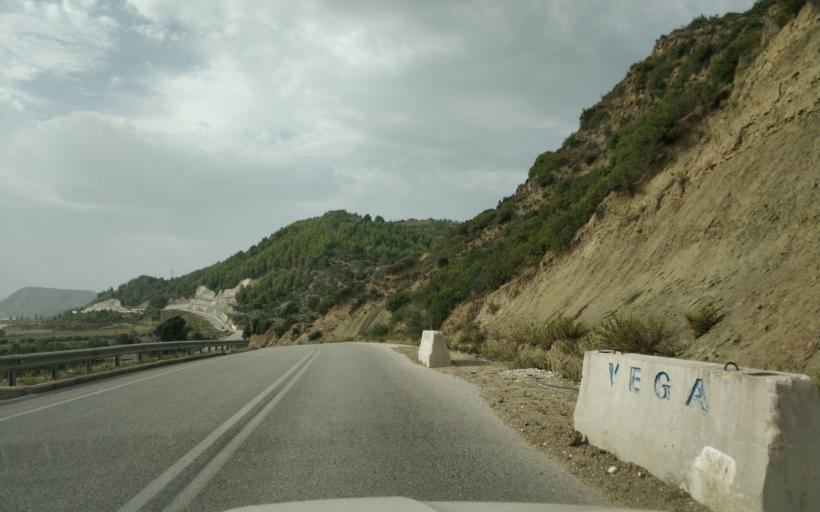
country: AL
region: Gjirokaster
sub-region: Rrethi i Tepelenes
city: Luftinje
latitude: 40.3804
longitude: 19.9024
